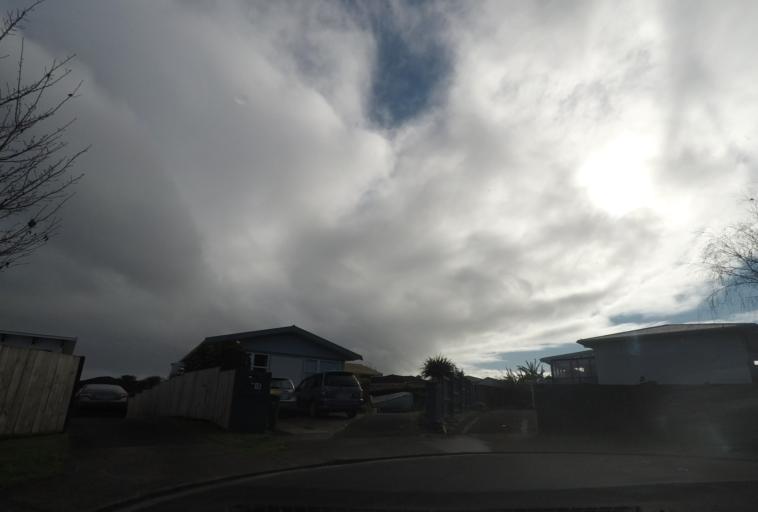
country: NZ
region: Auckland
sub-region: Auckland
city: Waitakere
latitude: -36.8996
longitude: 174.6599
